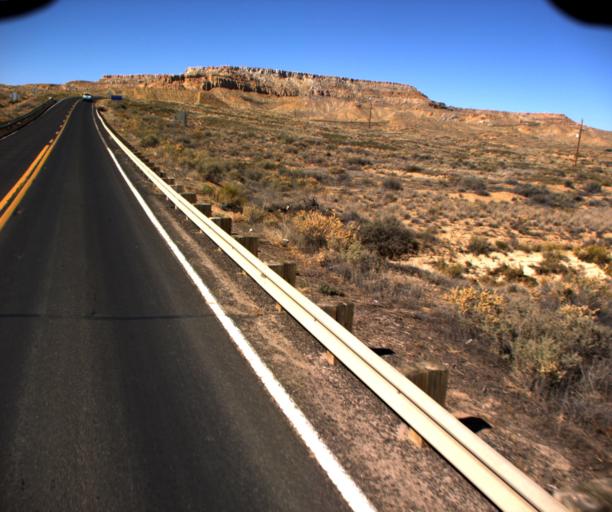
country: US
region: Arizona
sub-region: Navajo County
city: First Mesa
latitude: 35.7939
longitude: -110.5076
